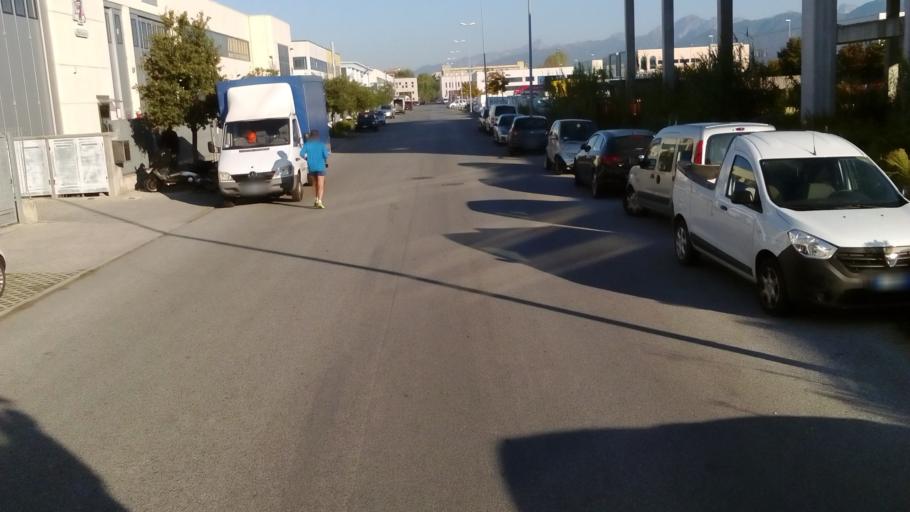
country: IT
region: Tuscany
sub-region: Provincia di Lucca
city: Viareggio
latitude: 43.8586
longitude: 10.2747
